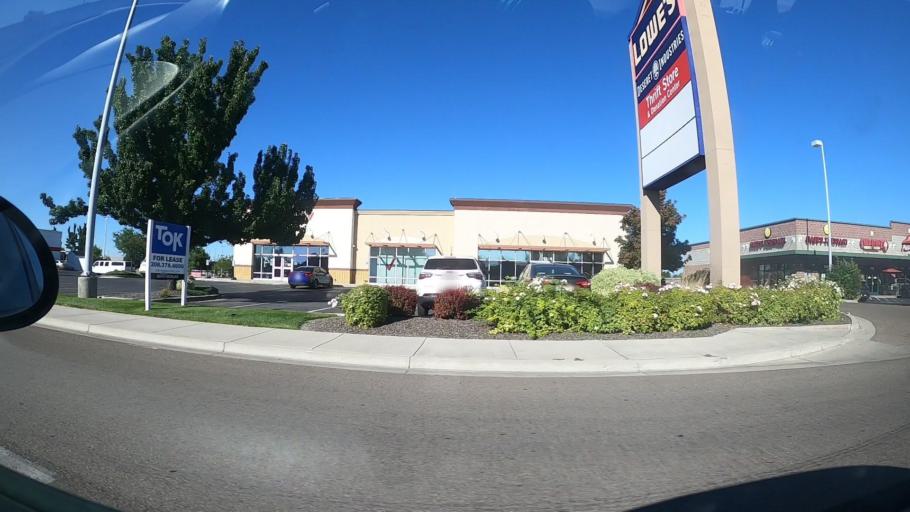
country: US
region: Idaho
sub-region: Canyon County
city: Nampa
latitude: 43.5998
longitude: -116.5946
